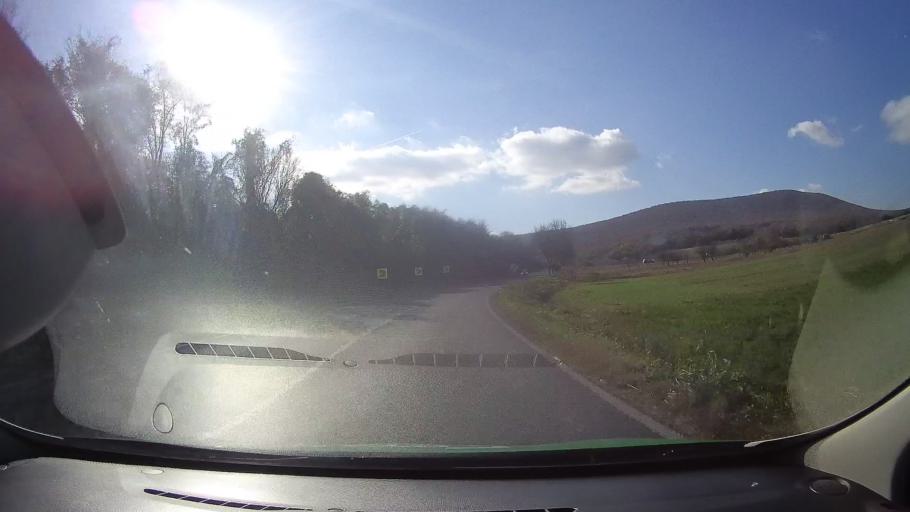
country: RO
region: Tulcea
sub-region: Oras Babadag
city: Babadag
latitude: 44.8772
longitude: 28.6914
